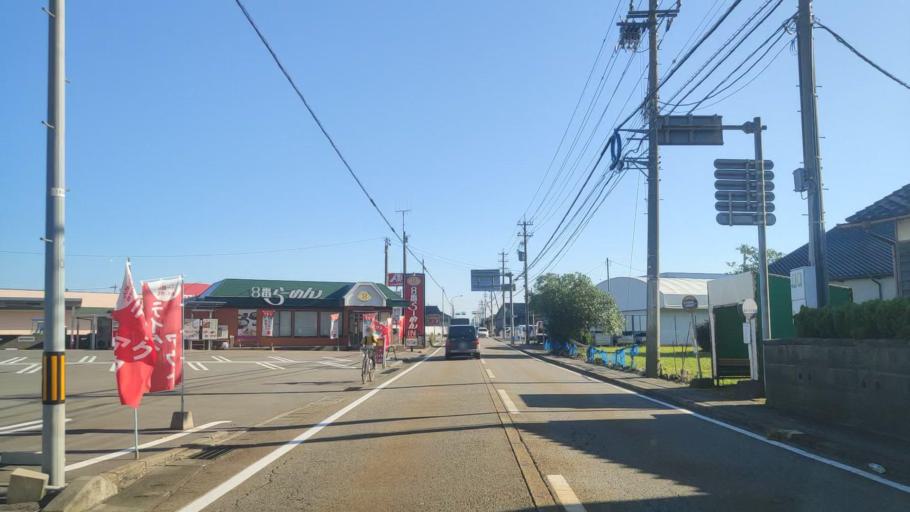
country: JP
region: Ishikawa
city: Tsubata
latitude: 36.7707
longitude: 136.7264
